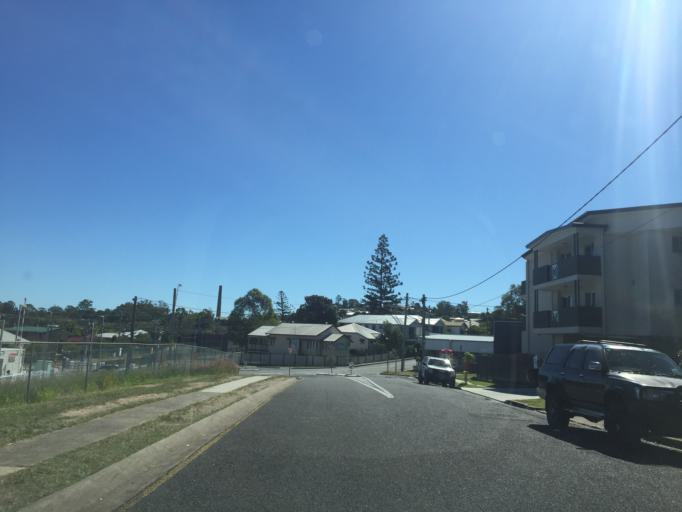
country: AU
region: Queensland
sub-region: Brisbane
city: Wilston
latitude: -27.4324
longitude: 153.0107
